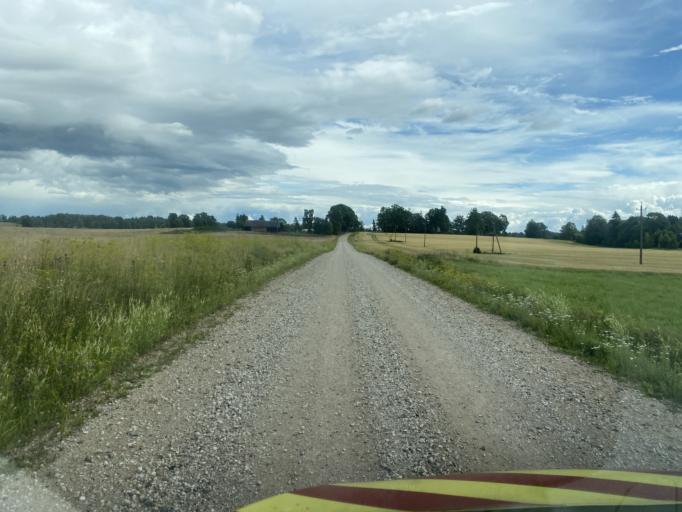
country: EE
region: Valgamaa
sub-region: Torva linn
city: Torva
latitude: 57.9416
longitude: 25.8982
